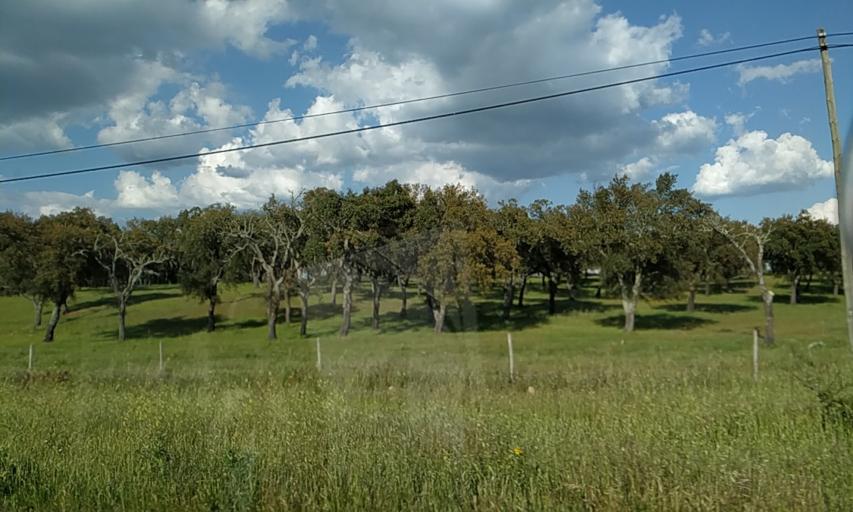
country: PT
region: Portalegre
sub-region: Portalegre
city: Urra
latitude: 39.1885
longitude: -7.4562
